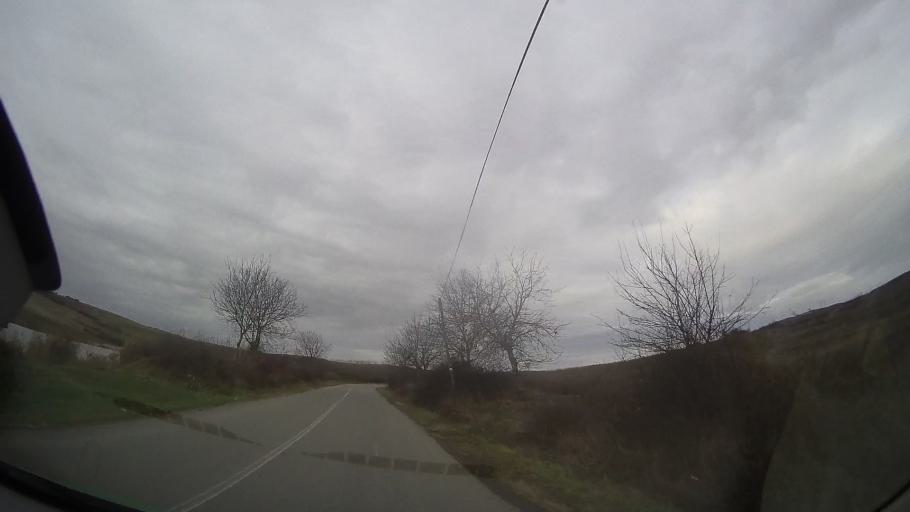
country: RO
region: Mures
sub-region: Comuna Faragau
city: Faragau
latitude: 46.7475
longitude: 24.5304
